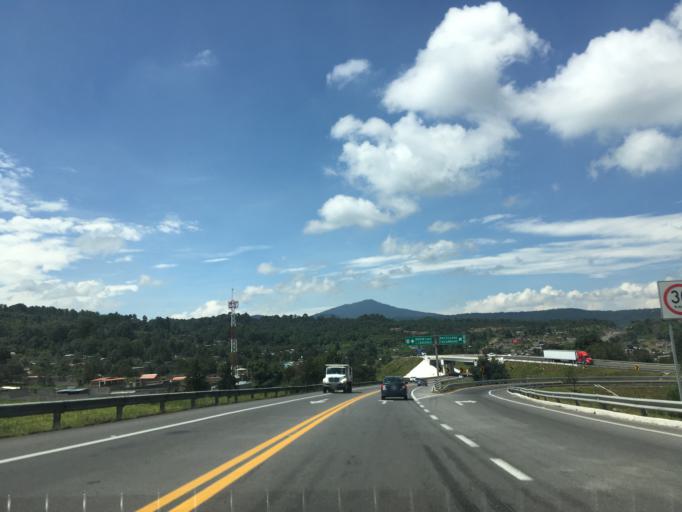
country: MX
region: Michoacan
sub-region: Patzcuaro
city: Colonia Vista Bella (Lomas del Peaje)
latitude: 19.4940
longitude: -101.5975
